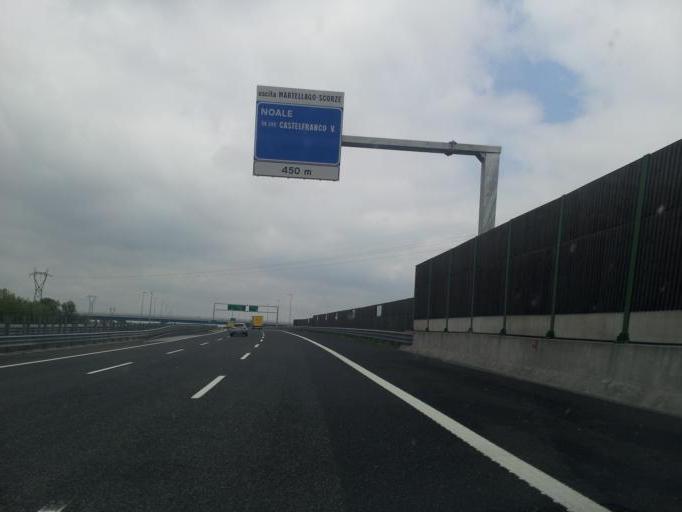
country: IT
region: Veneto
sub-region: Provincia di Venezia
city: Martellago
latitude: 45.5542
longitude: 12.1493
